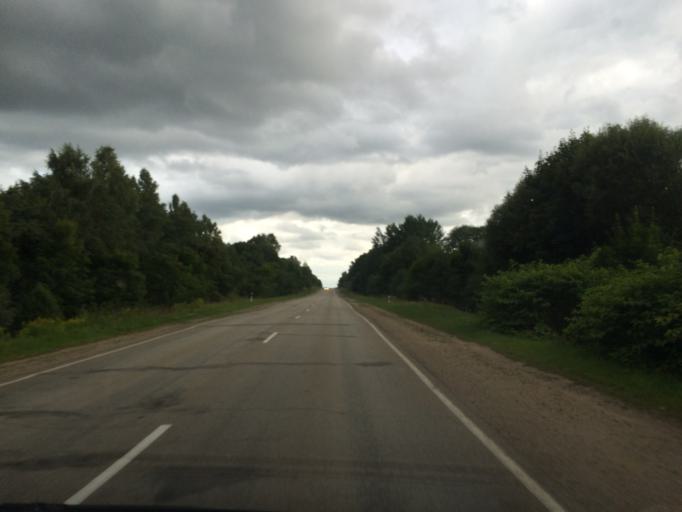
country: LV
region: Rezekne
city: Rezekne
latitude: 56.5657
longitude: 27.3670
